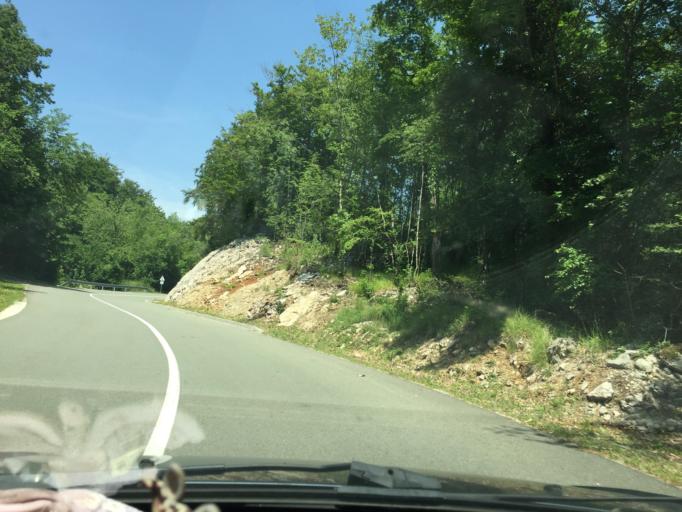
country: HR
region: Primorsko-Goranska
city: Matulji
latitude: 45.4089
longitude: 14.2531
